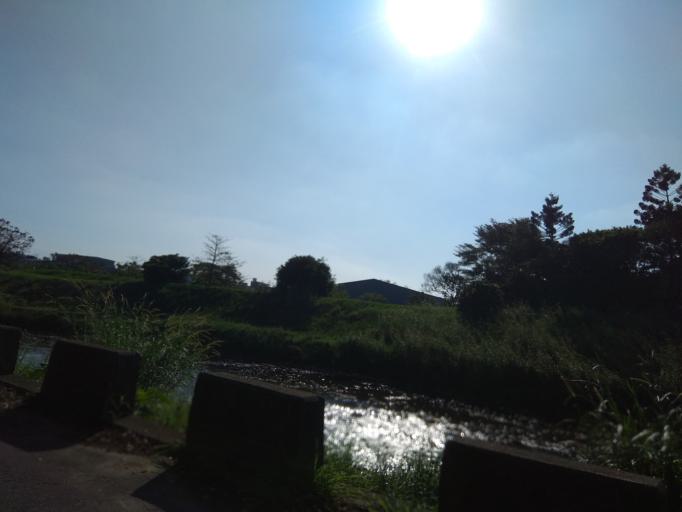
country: TW
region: Taiwan
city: Taoyuan City
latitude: 25.0638
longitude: 121.2099
